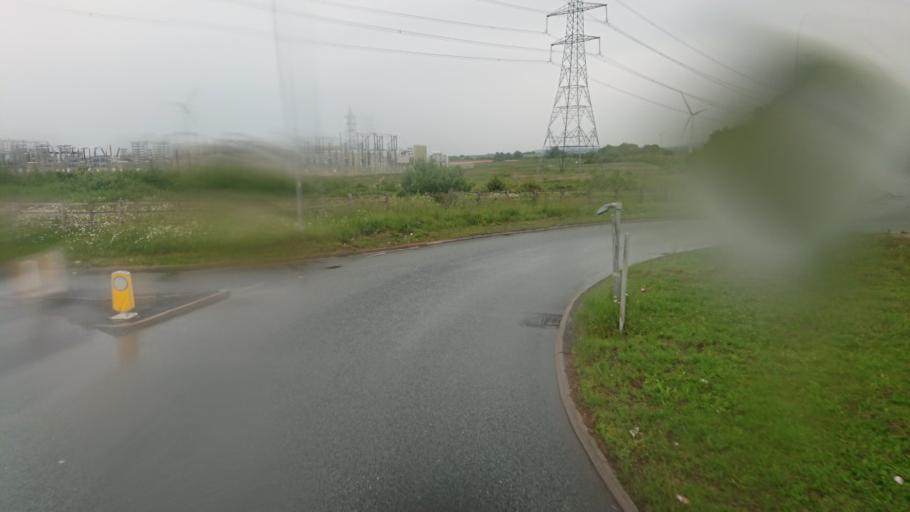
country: GB
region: England
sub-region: Lancashire
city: Morecambe
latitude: 54.0334
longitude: -2.8835
